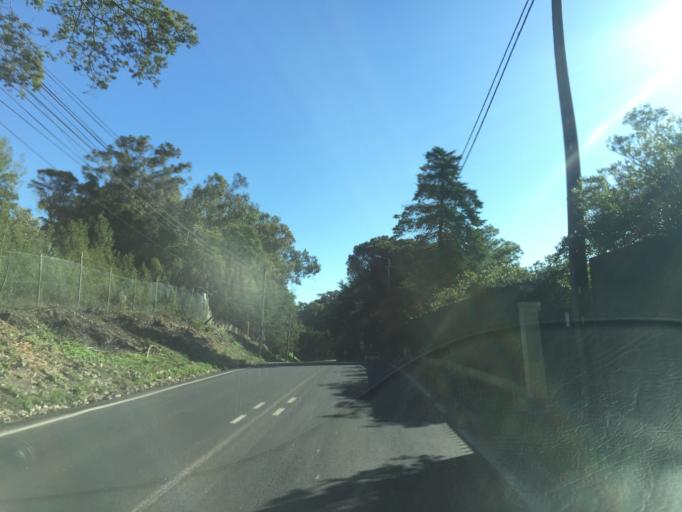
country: PT
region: Lisbon
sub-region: Sintra
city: Belas
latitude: 38.7993
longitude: -9.2735
